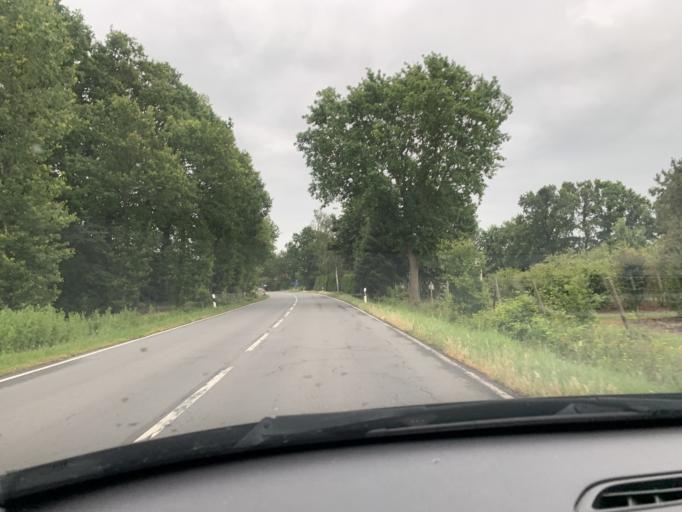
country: DE
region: Lower Saxony
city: Westerstede
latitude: 53.2542
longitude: 7.9616
